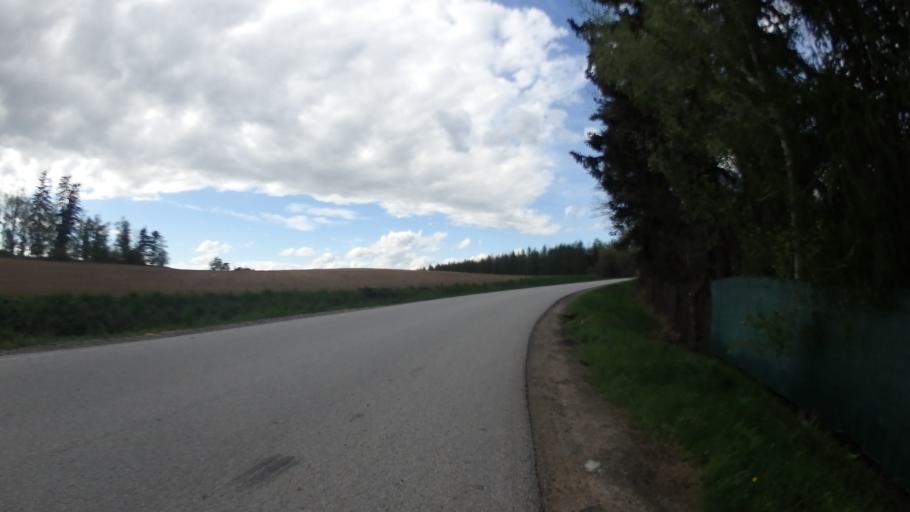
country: CZ
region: Vysocina
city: Merin
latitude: 49.3672
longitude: 15.8997
